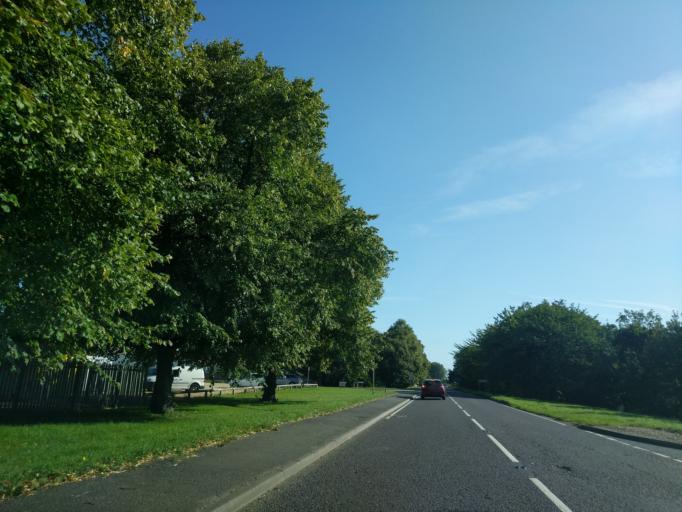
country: GB
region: England
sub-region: Lincolnshire
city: Bourne
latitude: 52.7687
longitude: -0.3618
